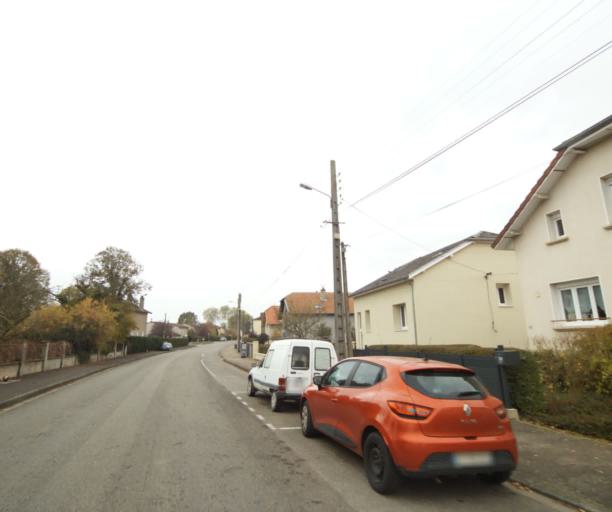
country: FR
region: Lorraine
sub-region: Departement de Meurthe-et-Moselle
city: Mancieulles
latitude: 49.2880
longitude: 5.8929
